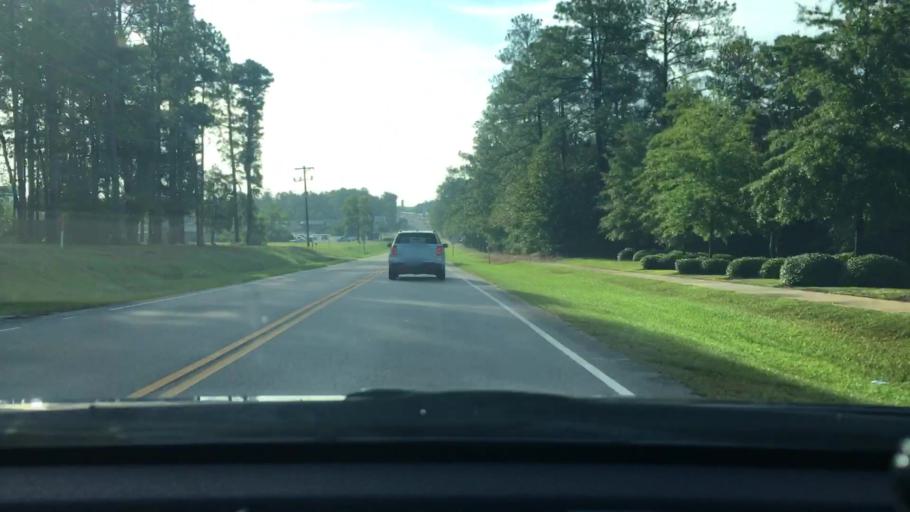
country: US
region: South Carolina
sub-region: Lexington County
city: Irmo
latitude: 34.1046
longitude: -81.1857
